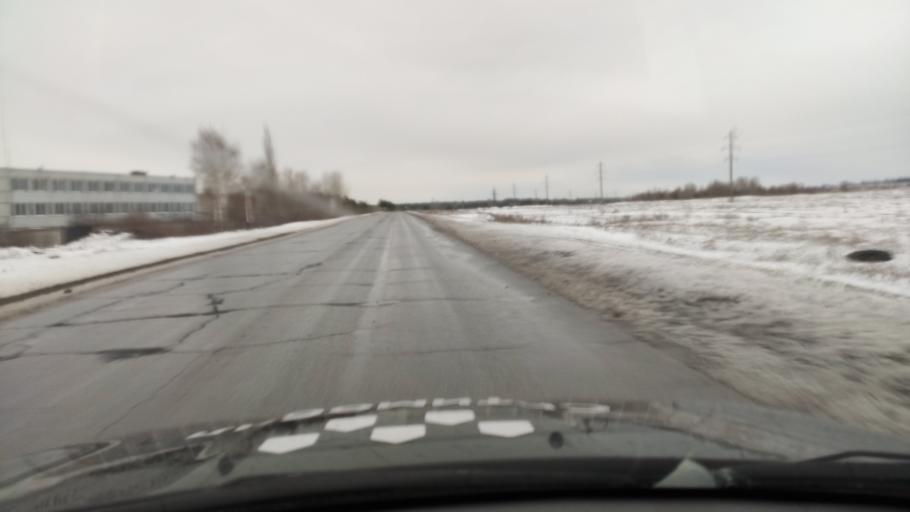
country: RU
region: Samara
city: Povolzhskiy
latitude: 53.5770
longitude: 49.6950
